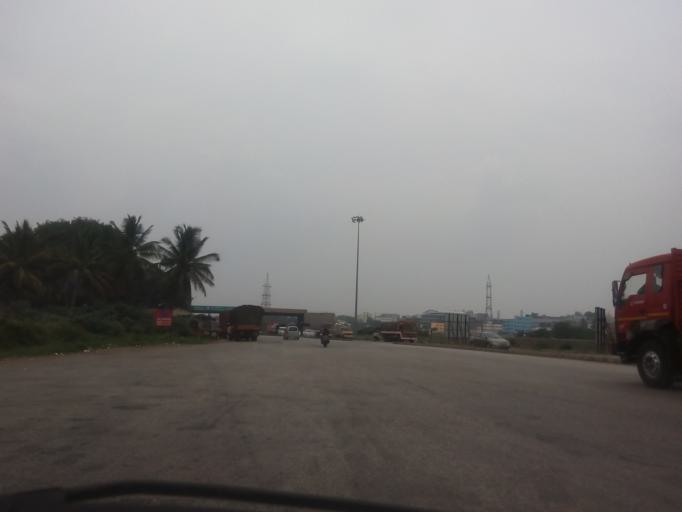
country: IN
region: Karnataka
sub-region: Bangalore Urban
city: Bangalore
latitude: 12.8587
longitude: 77.6569
